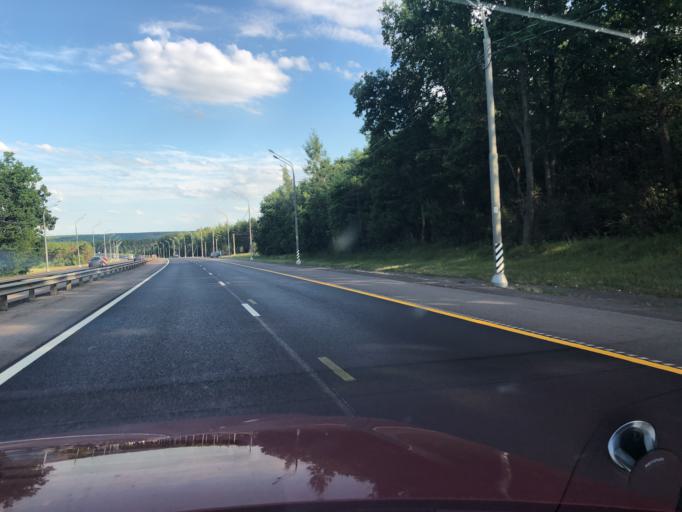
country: RU
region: Lipetsk
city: Zadonsk
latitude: 52.3837
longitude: 38.8708
